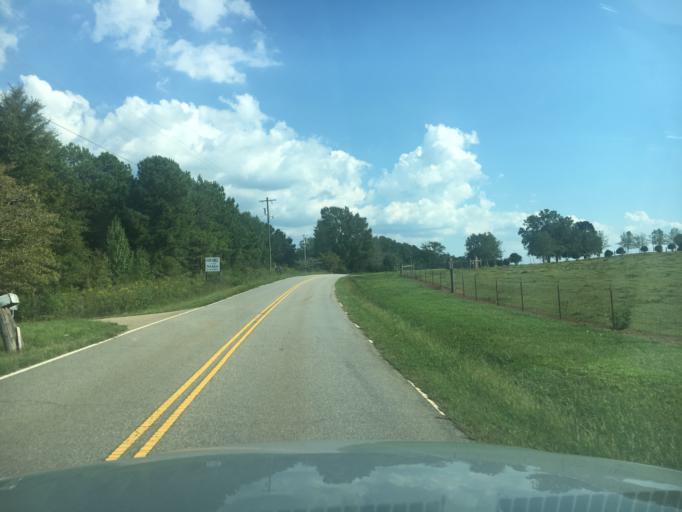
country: US
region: South Carolina
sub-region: Pickens County
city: Liberty
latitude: 34.7333
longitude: -82.6426
